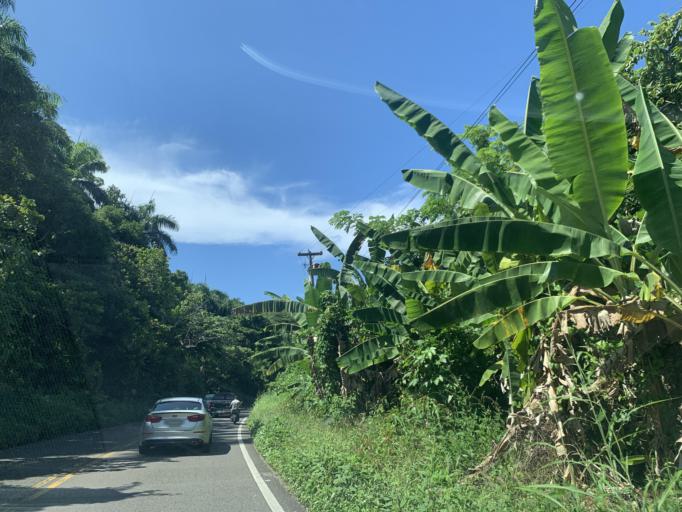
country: DO
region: Maria Trinidad Sanchez
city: Cabrera
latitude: 19.6575
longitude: -69.9375
